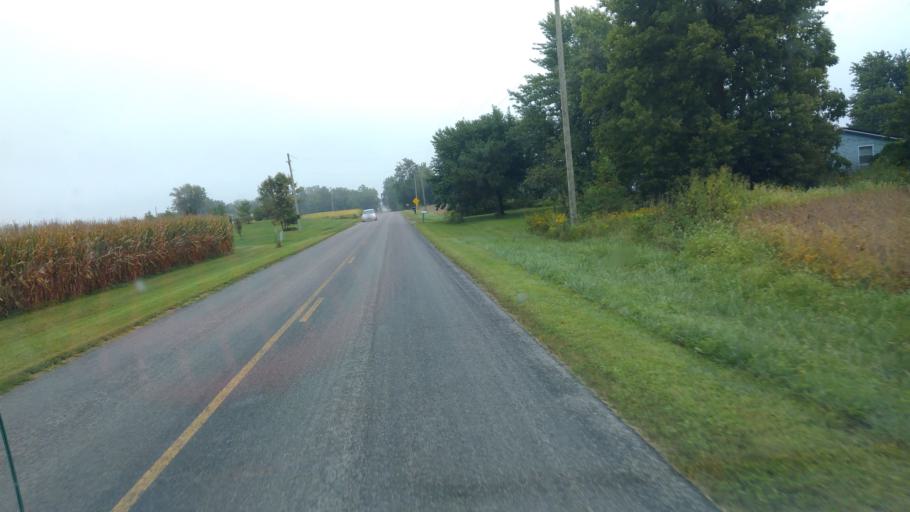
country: US
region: Ohio
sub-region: Union County
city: Richwood
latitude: 40.4865
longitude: -83.3791
